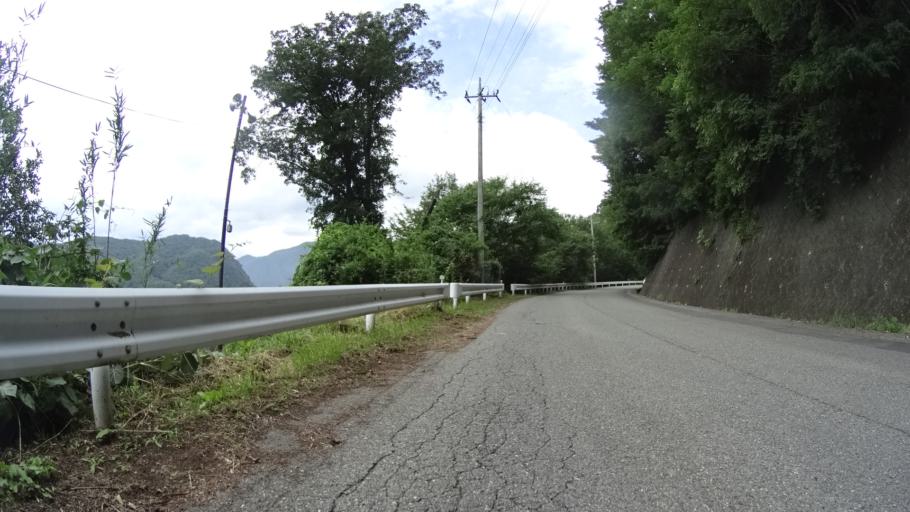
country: JP
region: Yamanashi
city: Nirasaki
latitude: 35.8575
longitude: 138.5218
